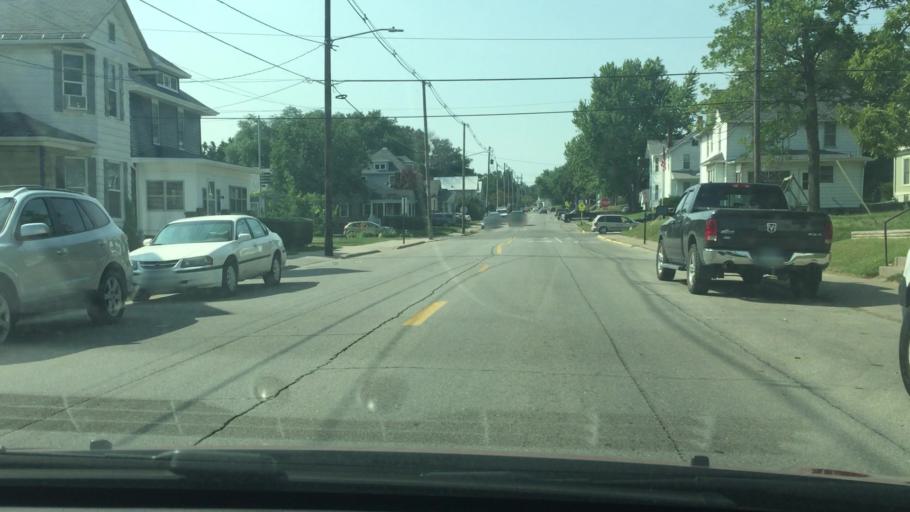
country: US
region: Iowa
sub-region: Muscatine County
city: Muscatine
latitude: 41.4267
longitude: -91.0477
